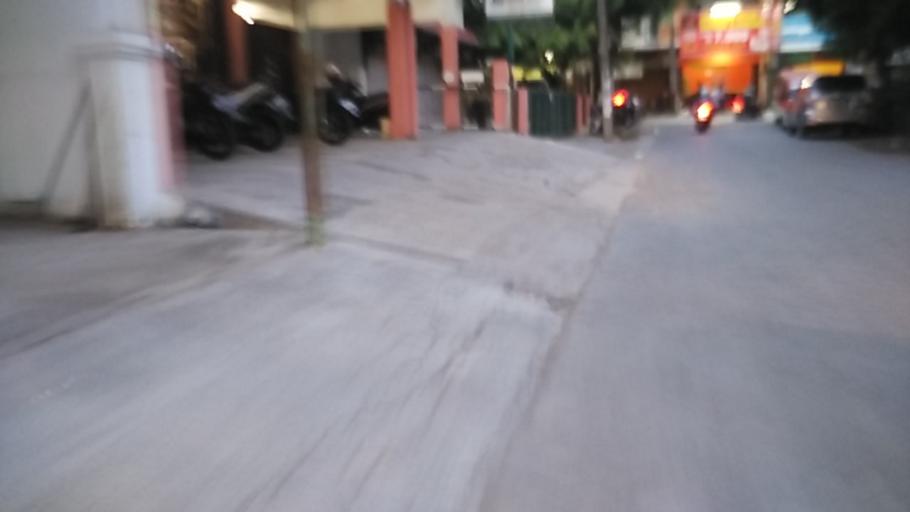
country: ID
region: Central Java
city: Semarang
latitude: -6.9829
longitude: 110.4588
